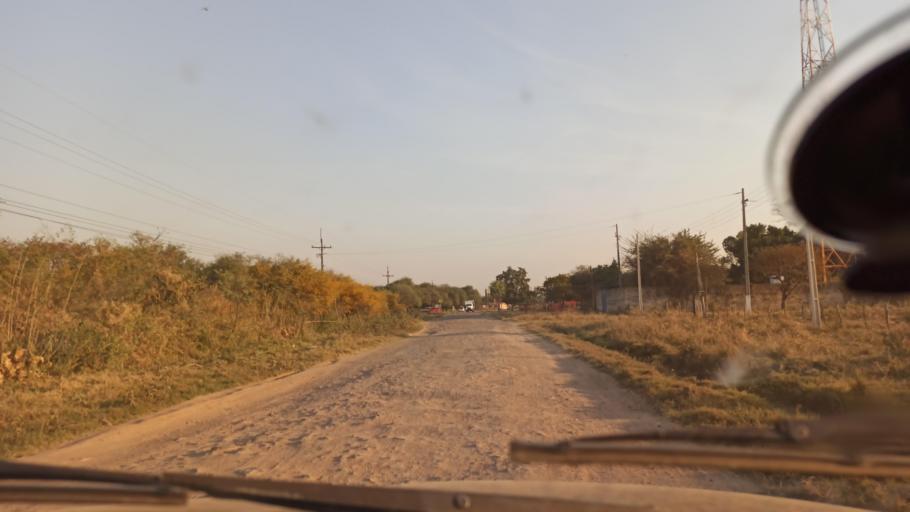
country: PY
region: Presidente Hayes
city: Nanawa
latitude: -25.2323
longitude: -57.6312
